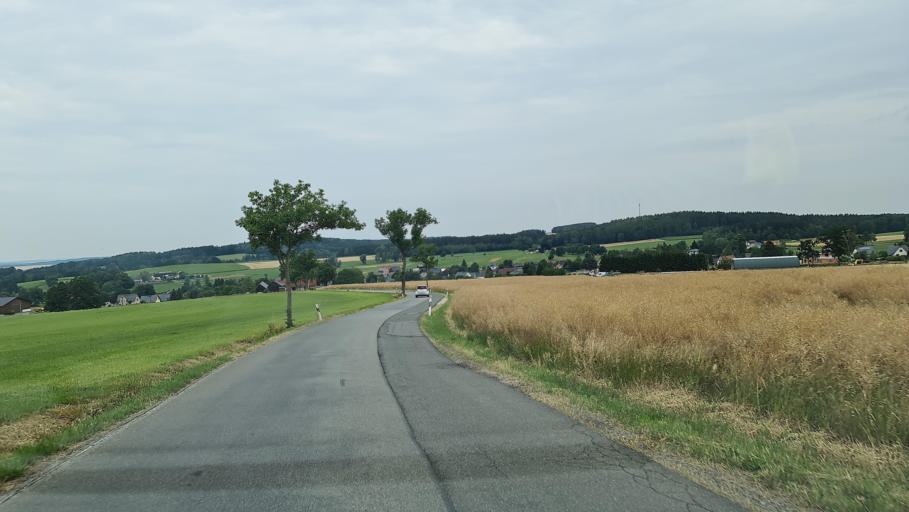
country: DE
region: Saxony
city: Rodewisch
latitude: 50.5501
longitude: 12.4627
